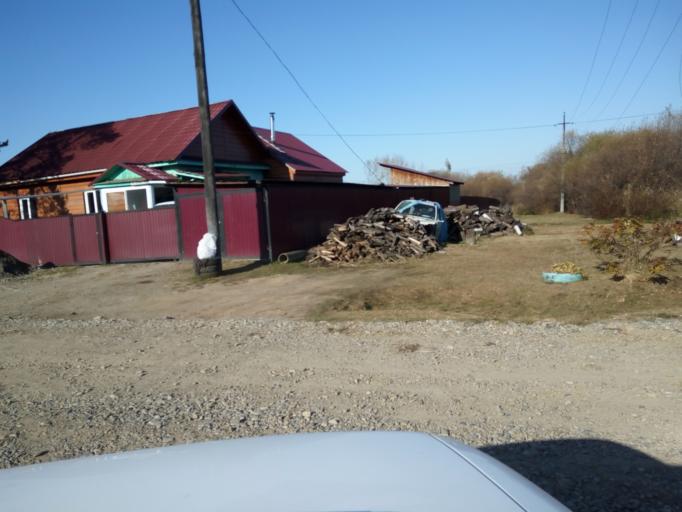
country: RU
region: Primorskiy
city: Lazo
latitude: 45.8711
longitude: 133.6442
